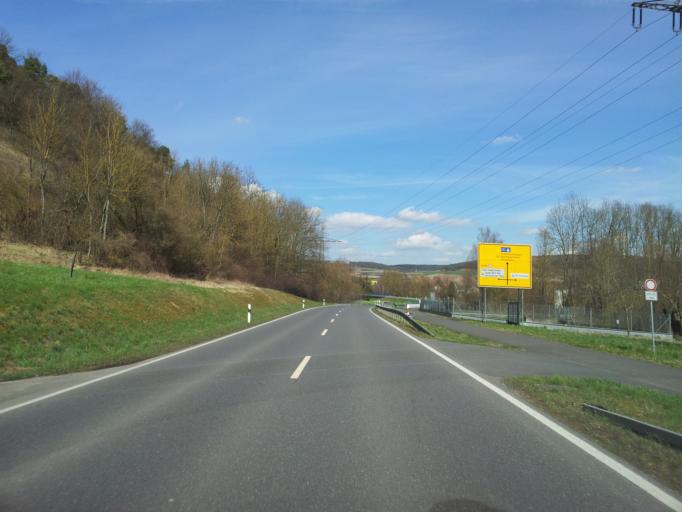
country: DE
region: Baden-Wuerttemberg
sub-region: Regierungsbezirk Stuttgart
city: Lauda-Konigshofen
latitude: 49.5395
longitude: 9.7218
